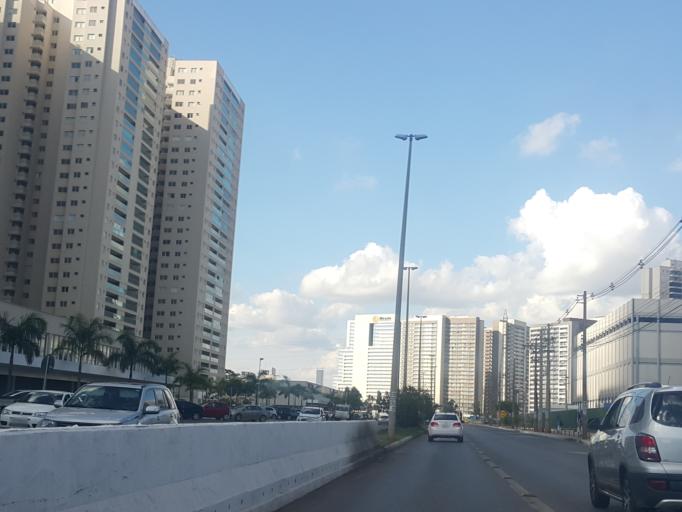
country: BR
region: Federal District
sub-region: Brasilia
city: Brasilia
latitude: -15.8356
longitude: -48.0484
